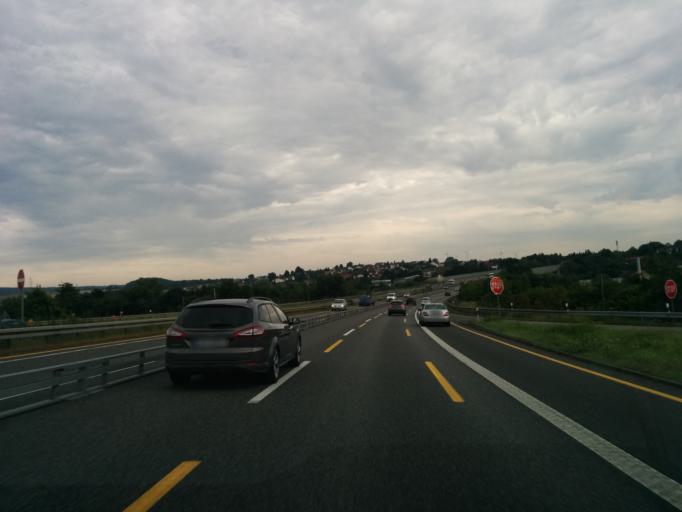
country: DE
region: Hesse
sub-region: Regierungsbezirk Kassel
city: Lohfelden
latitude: 51.2968
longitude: 9.5624
